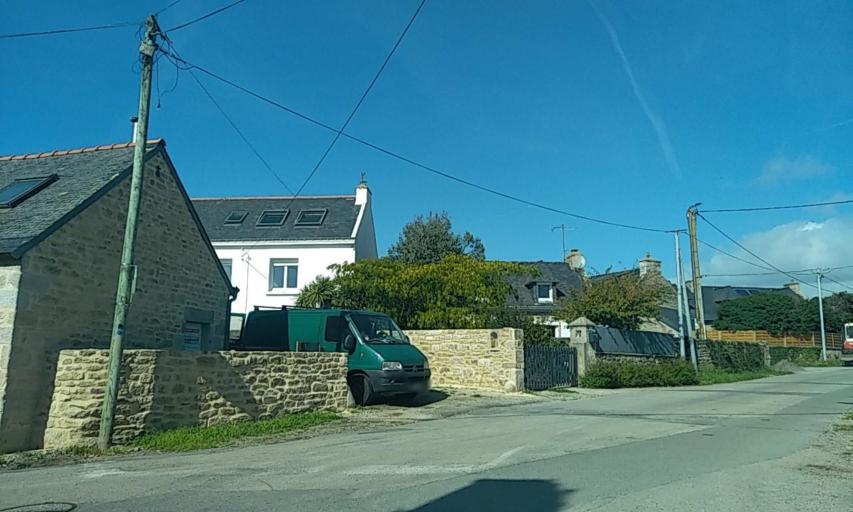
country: FR
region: Brittany
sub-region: Departement du Morbihan
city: Ploemeur
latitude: 47.7153
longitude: -3.4543
